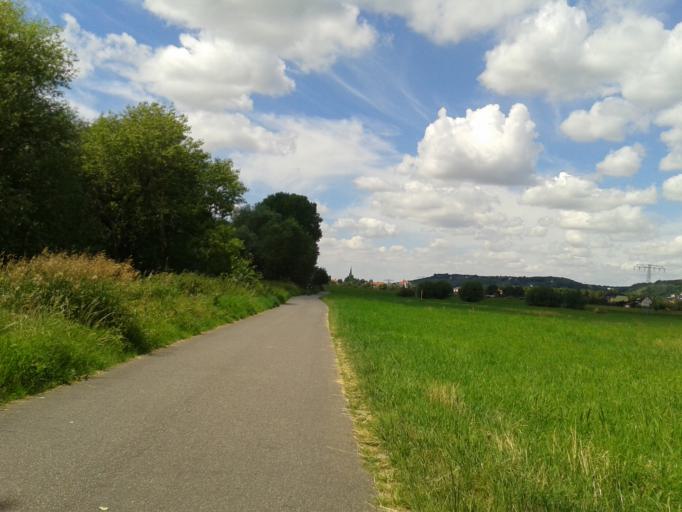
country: DE
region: Saxony
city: Radebeul
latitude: 51.0949
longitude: 13.6509
